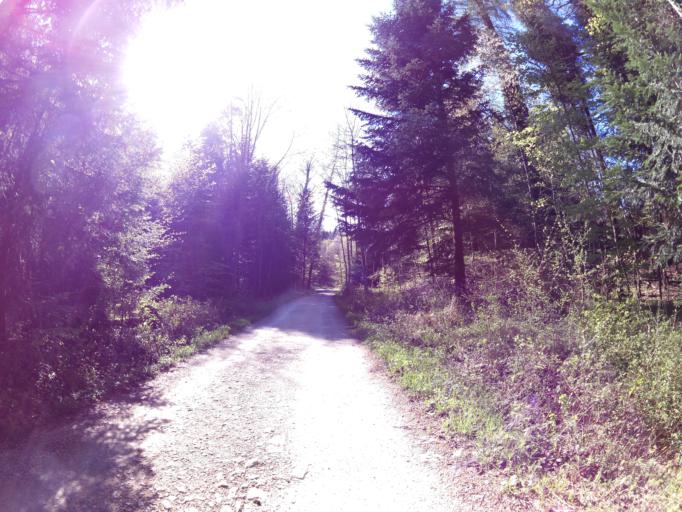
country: CH
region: Aargau
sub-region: Bezirk Aarau
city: Aarau
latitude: 47.4062
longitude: 8.0283
